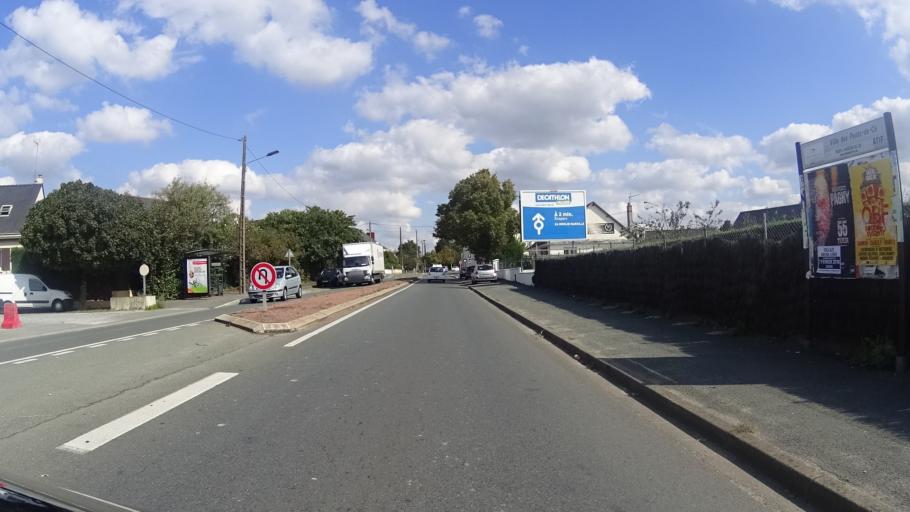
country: FR
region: Pays de la Loire
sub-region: Departement de Maine-et-Loire
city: Les Ponts-de-Ce
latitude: 47.4372
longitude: -0.5141
